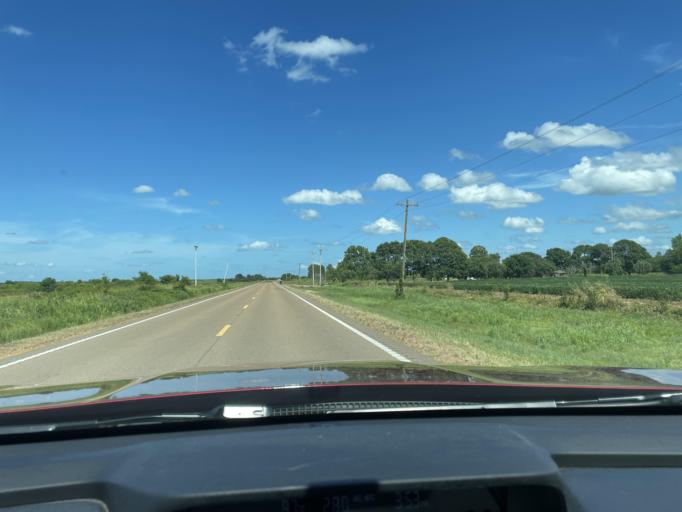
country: US
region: Mississippi
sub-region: Humphreys County
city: Belzoni
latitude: 33.1843
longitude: -90.6686
